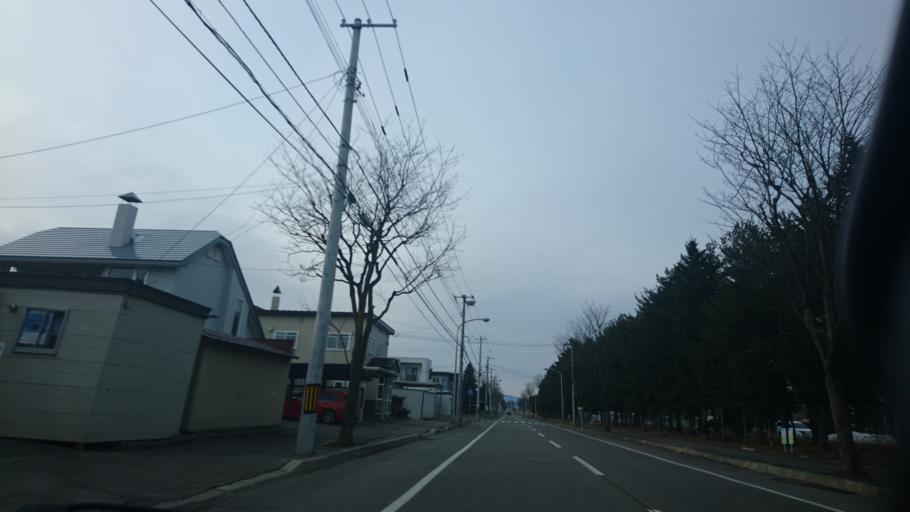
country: JP
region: Hokkaido
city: Otofuke
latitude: 42.9926
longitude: 143.1924
